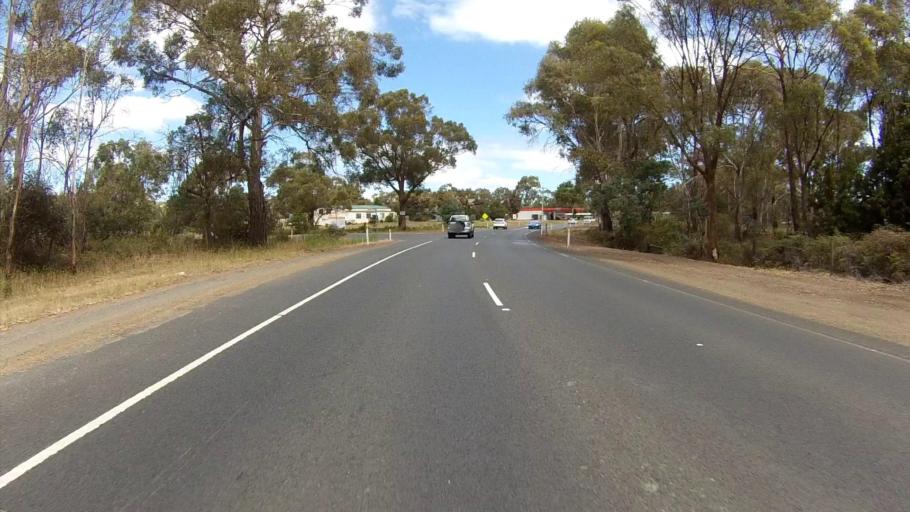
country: AU
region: Tasmania
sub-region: Sorell
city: Sorell
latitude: -42.8470
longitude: 147.6273
